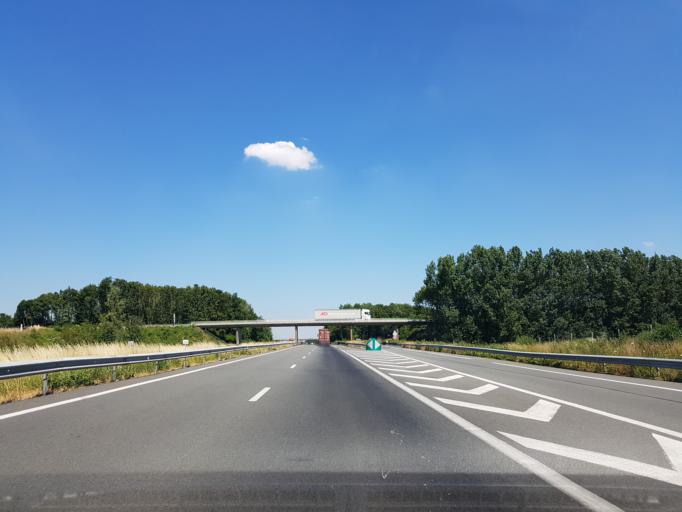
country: FR
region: Nord-Pas-de-Calais
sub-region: Departement du Nord
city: Marcoing
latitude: 50.0677
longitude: 3.1777
